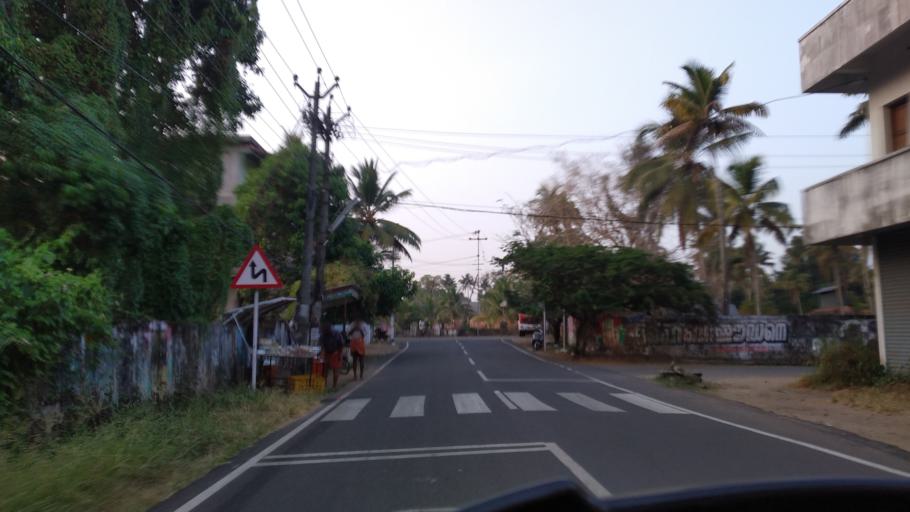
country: IN
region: Kerala
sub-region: Ernakulam
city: Elur
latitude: 10.1354
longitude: 76.2315
